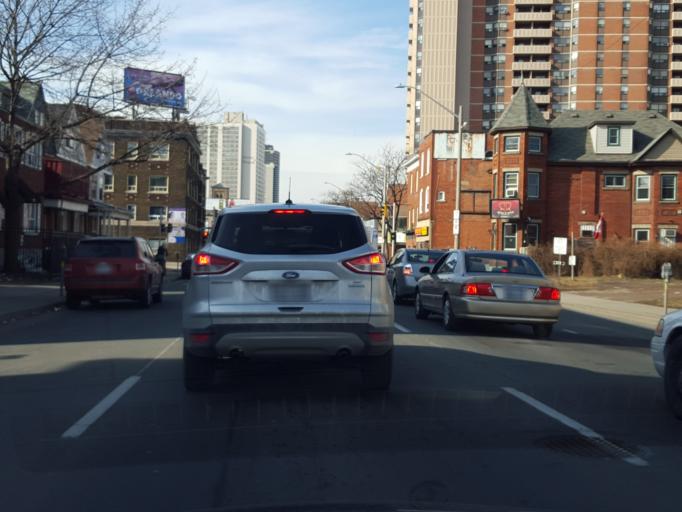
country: CA
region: Ontario
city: Hamilton
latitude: 43.2524
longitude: -79.8521
